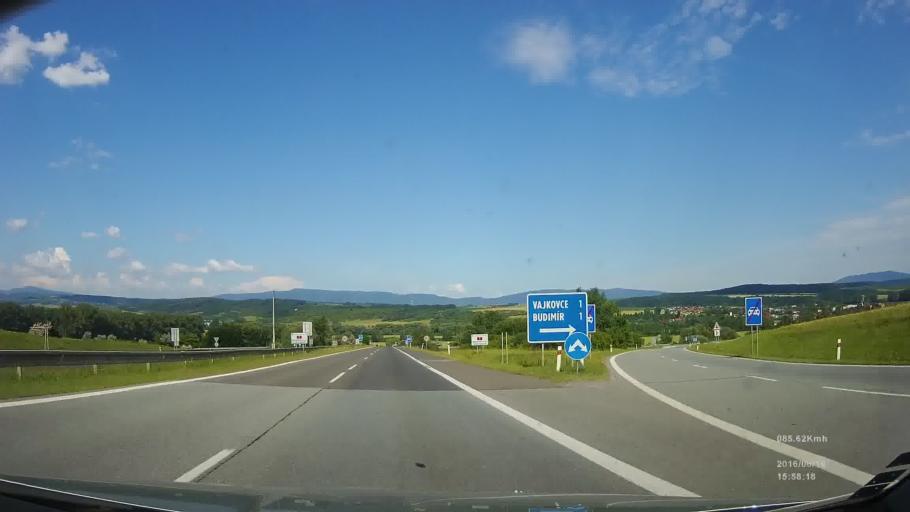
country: SK
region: Kosicky
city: Kosice
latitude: 48.7875
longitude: 21.3046
